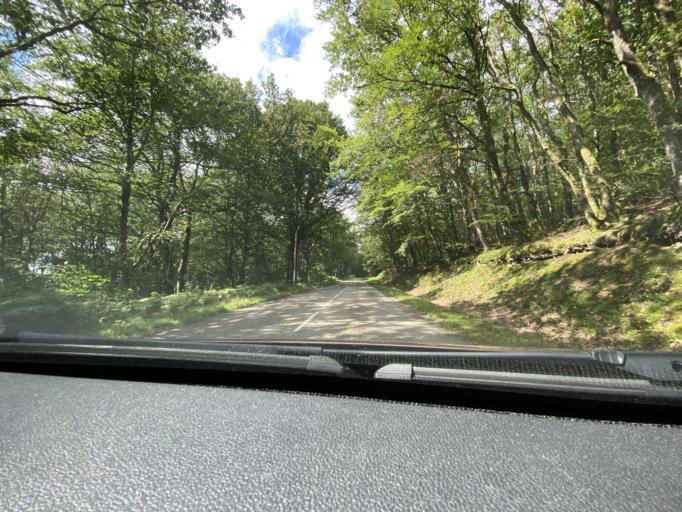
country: FR
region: Bourgogne
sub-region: Departement de la Cote-d'Or
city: Saulieu
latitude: 47.2503
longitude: 4.0721
